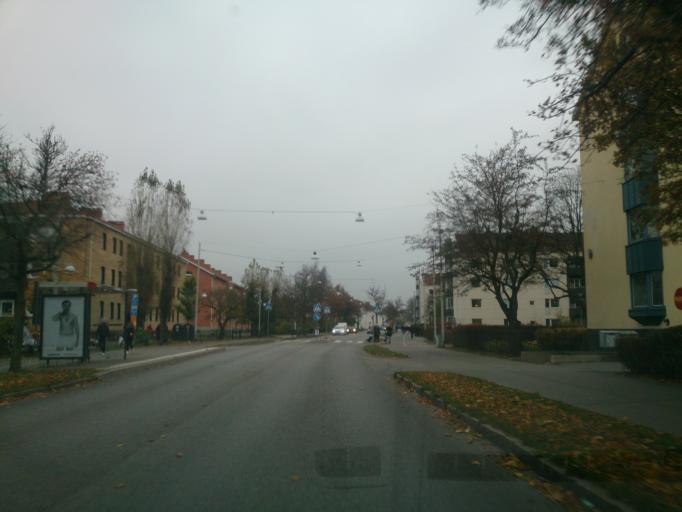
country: SE
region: OEstergoetland
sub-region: Norrkopings Kommun
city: Norrkoping
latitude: 58.5777
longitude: 16.1969
